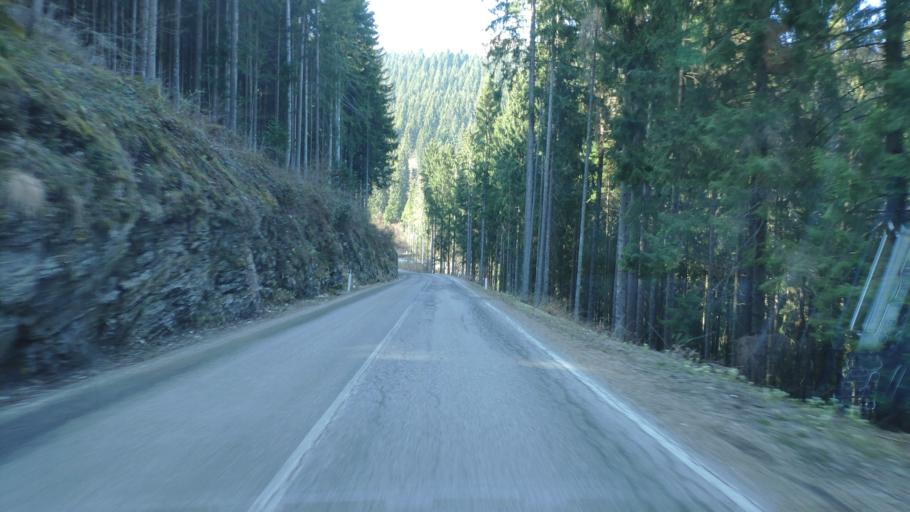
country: IT
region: Veneto
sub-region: Provincia di Vicenza
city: Enego
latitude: 45.9363
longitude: 11.6995
